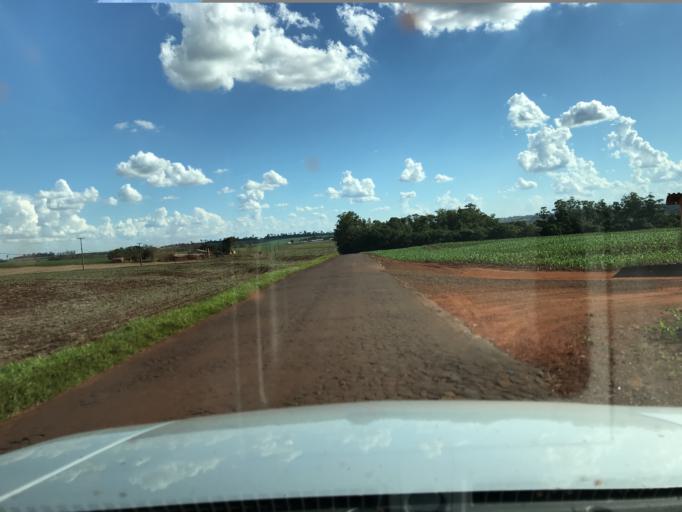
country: BR
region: Parana
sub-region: Palotina
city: Palotina
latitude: -24.2441
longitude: -53.7910
